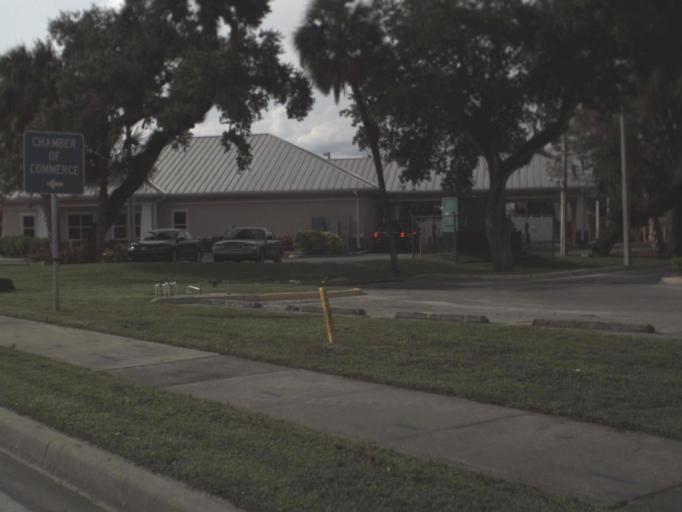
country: US
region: Florida
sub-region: Hendry County
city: LaBelle
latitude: 26.7618
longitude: -81.4364
